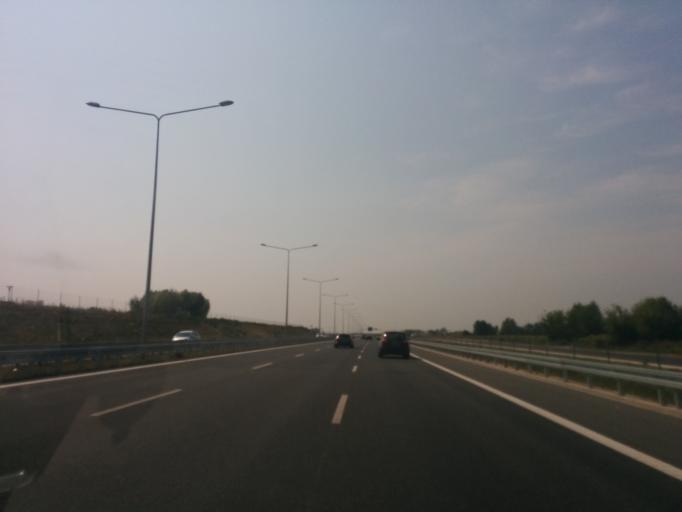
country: PL
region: Masovian Voivodeship
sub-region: Powiat pruszkowski
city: Nowe Grocholice
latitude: 52.1514
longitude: 20.8954
